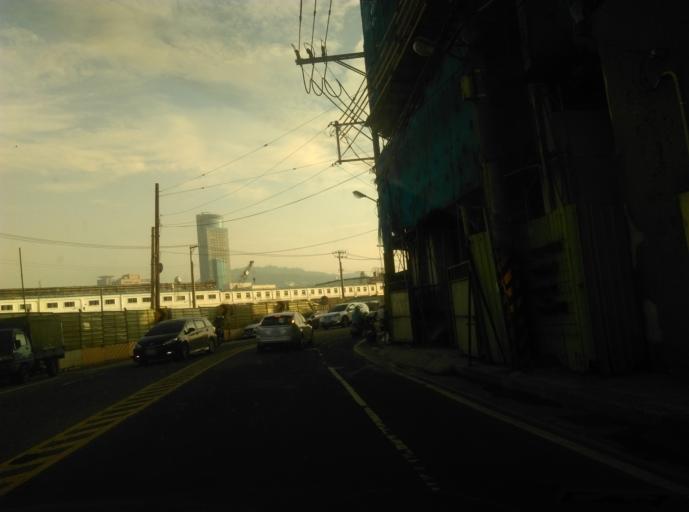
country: TW
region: Taiwan
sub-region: Keelung
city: Keelung
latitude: 25.1370
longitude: 121.7410
